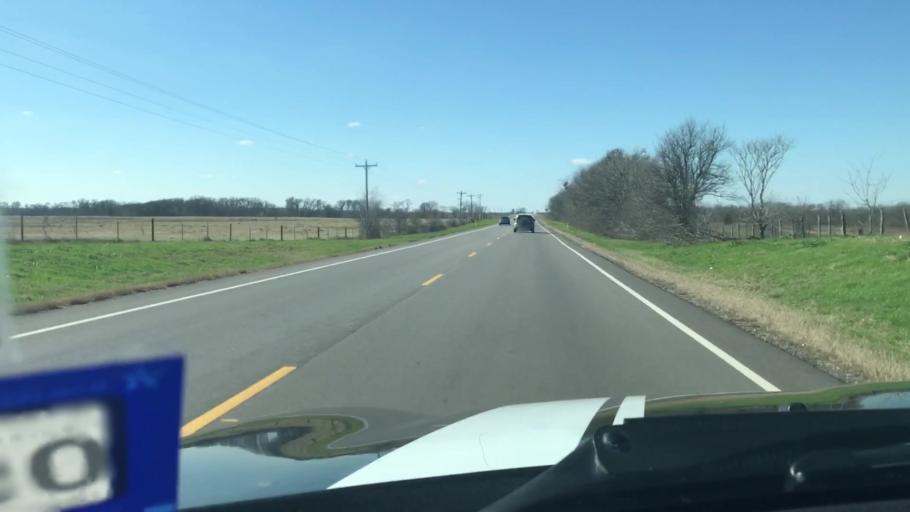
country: US
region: Texas
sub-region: Robertson County
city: Hearne
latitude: 30.8819
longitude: -96.6330
